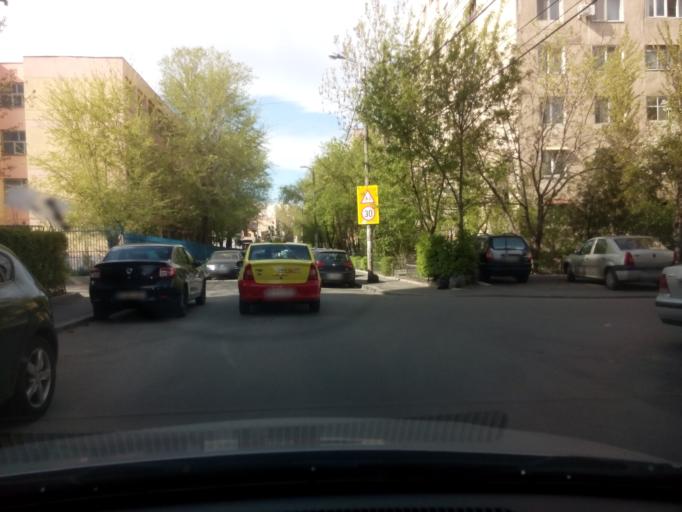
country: RO
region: Ilfov
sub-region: Comuna Fundeni-Dobroesti
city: Fundeni
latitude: 44.4382
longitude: 26.1557
